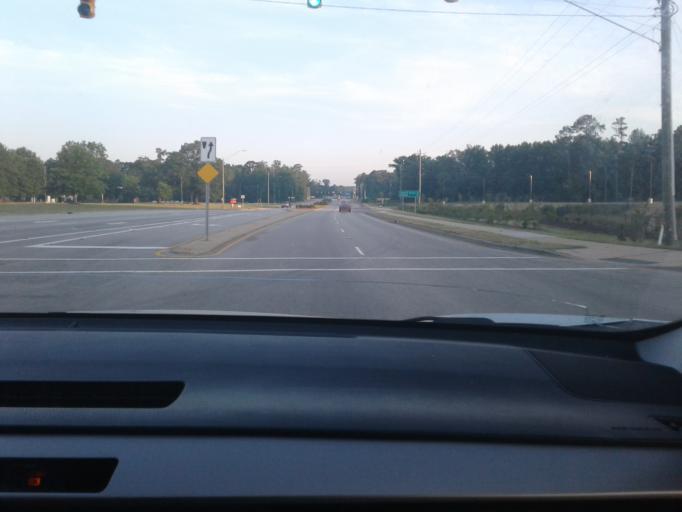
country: US
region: North Carolina
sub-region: Harnett County
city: Lillington
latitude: 35.4200
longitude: -78.8073
